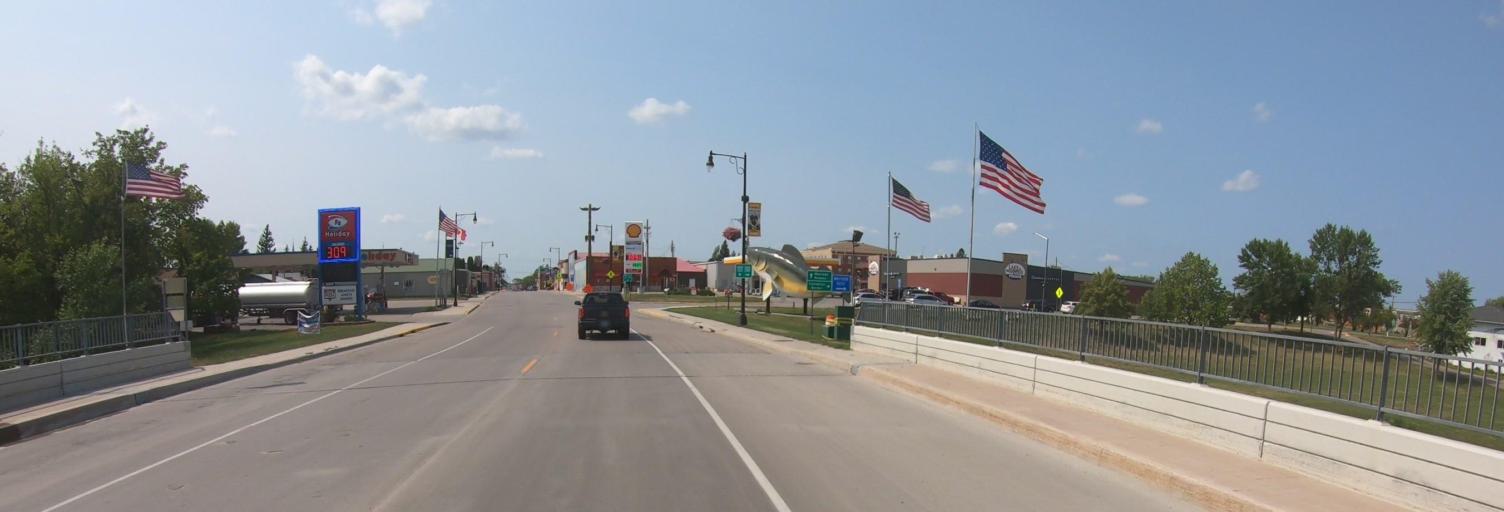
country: US
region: Minnesota
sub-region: Lake of the Woods County
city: Baudette
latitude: 48.7123
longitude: -94.5970
